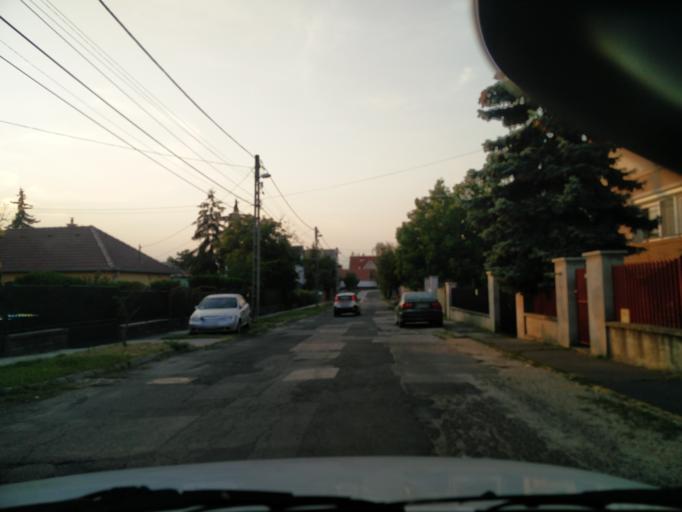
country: HU
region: Budapest
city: Budapest XXIII. keruelet
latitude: 47.4047
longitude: 19.0874
